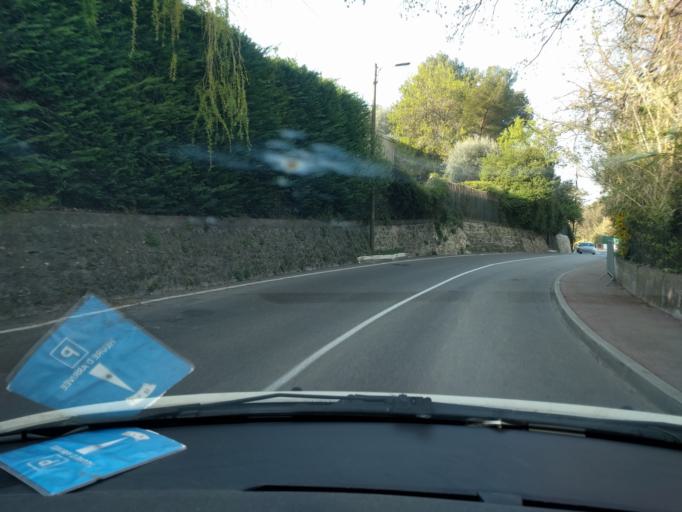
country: FR
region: Provence-Alpes-Cote d'Azur
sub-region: Departement des Alpes-Maritimes
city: Mougins
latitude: 43.5883
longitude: 6.9994
